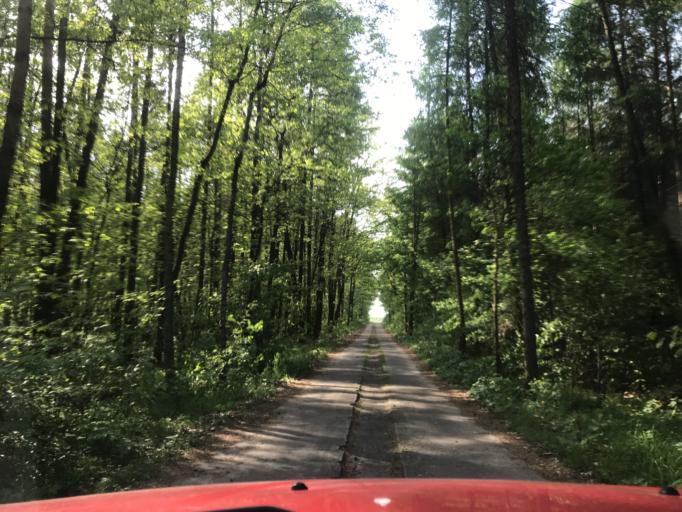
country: PL
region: Greater Poland Voivodeship
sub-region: Powiat kaliski
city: Stawiszyn
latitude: 51.9412
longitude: 18.1542
